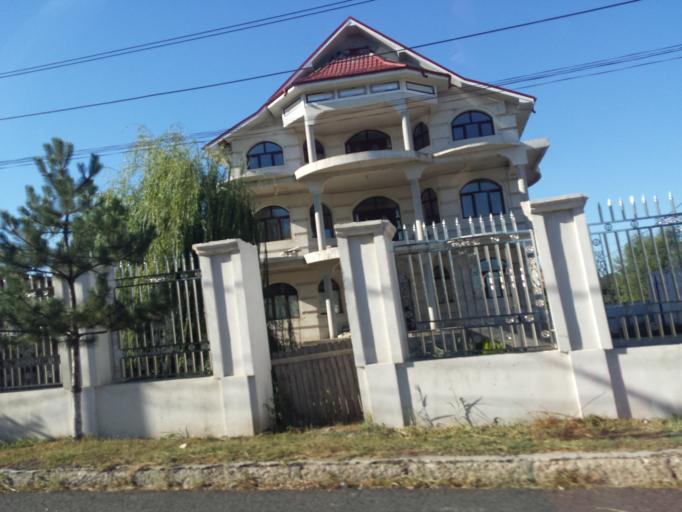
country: RO
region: Ialomita
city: Tandarei
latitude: 44.6442
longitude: 27.6479
